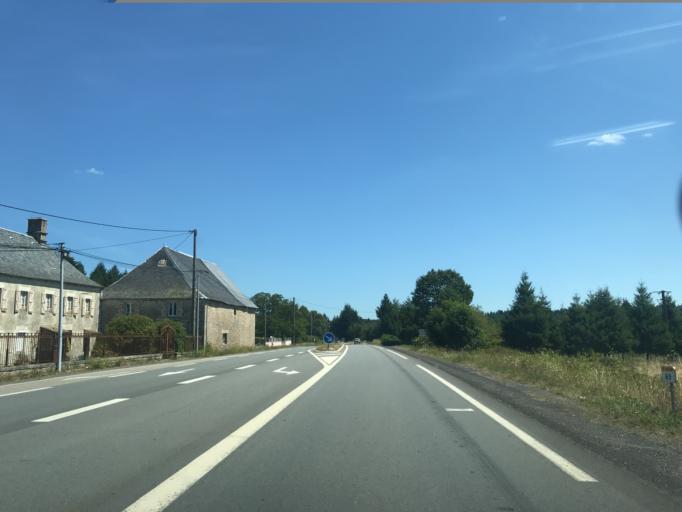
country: FR
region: Limousin
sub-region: Departement de la Correze
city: Correze
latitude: 45.3343
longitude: 1.9148
